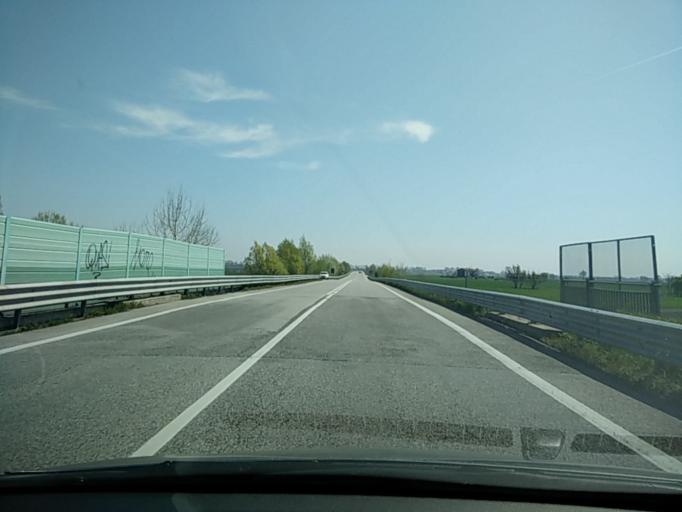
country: IT
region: Veneto
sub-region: Provincia di Venezia
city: Musile di Piave
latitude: 45.5976
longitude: 12.5312
